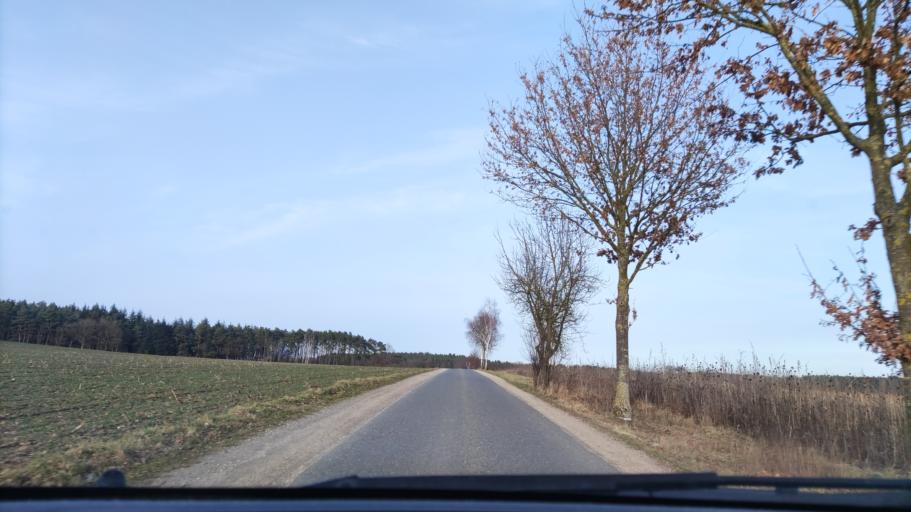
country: DE
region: Lower Saxony
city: Dahlenburg
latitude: 53.1976
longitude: 10.6983
